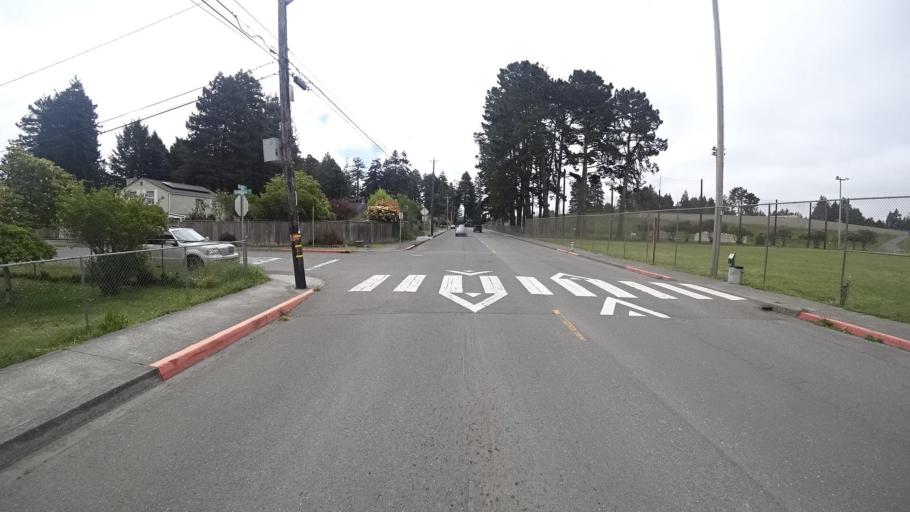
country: US
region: California
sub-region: Humboldt County
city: Cutten
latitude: 40.7752
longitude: -124.1421
